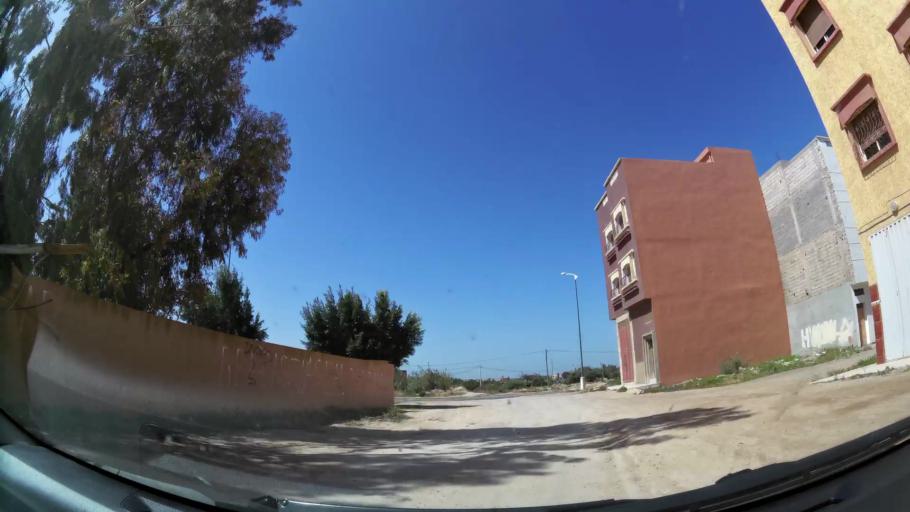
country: MA
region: Souss-Massa-Draa
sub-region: Inezgane-Ait Mellou
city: Inezgane
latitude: 30.3281
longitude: -9.5090
